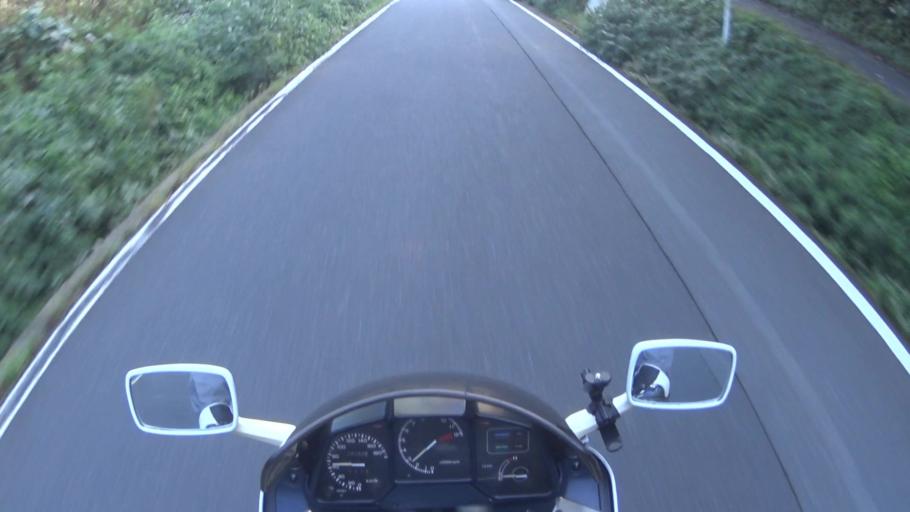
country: JP
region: Kyoto
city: Miyazu
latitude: 35.7017
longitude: 135.0699
